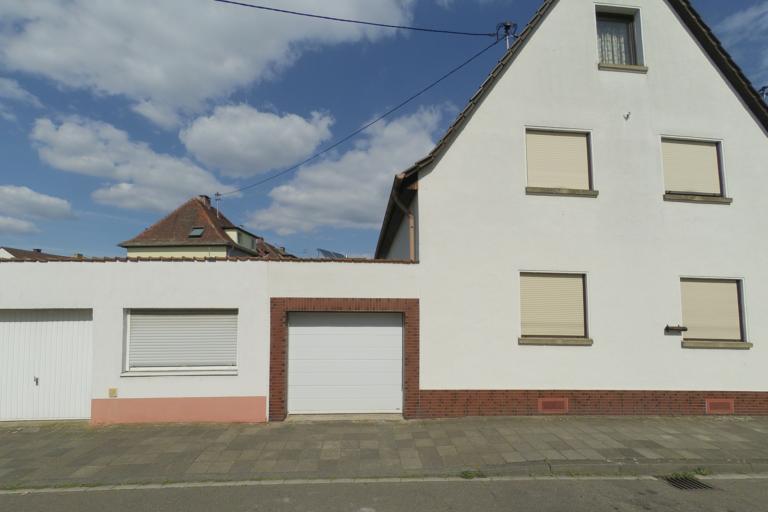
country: DE
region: Rheinland-Pfalz
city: Gartenstadt
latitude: 49.4476
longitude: 8.4170
